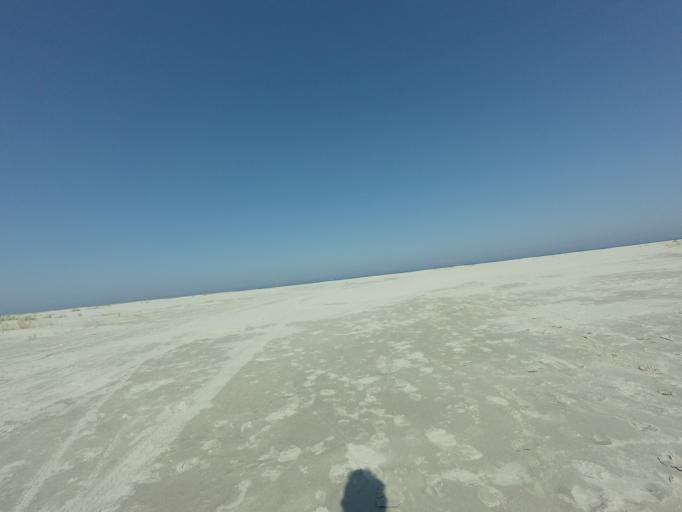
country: NL
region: Friesland
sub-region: Gemeente Schiermonnikoog
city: Schiermonnikoog
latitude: 53.5040
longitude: 6.2448
